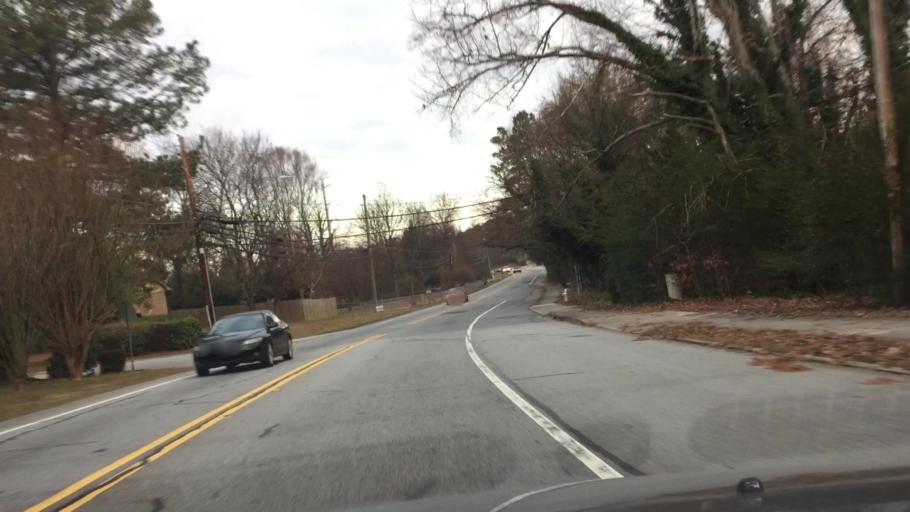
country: US
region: Georgia
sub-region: DeKalb County
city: Doraville
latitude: 33.9495
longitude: -84.2715
